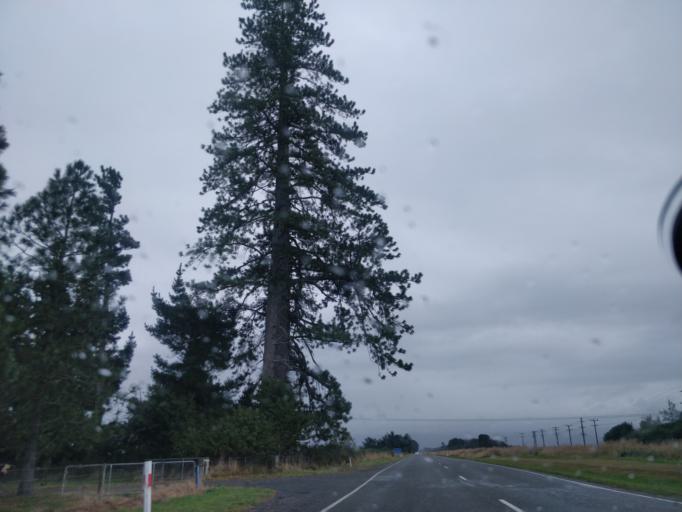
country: NZ
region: Canterbury
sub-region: Selwyn District
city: Darfield
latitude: -43.3848
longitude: 172.0123
